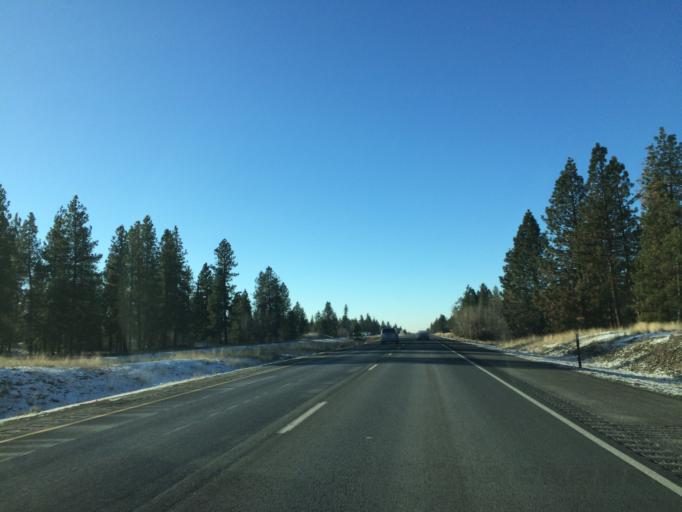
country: US
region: Washington
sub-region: Spokane County
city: Medical Lake
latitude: 47.4738
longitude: -117.7360
